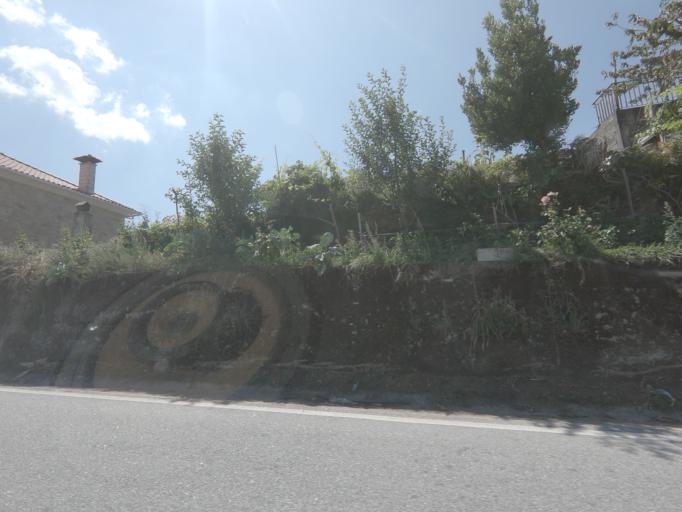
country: PT
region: Viseu
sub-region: Tarouca
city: Tarouca
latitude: 40.9895
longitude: -7.7804
